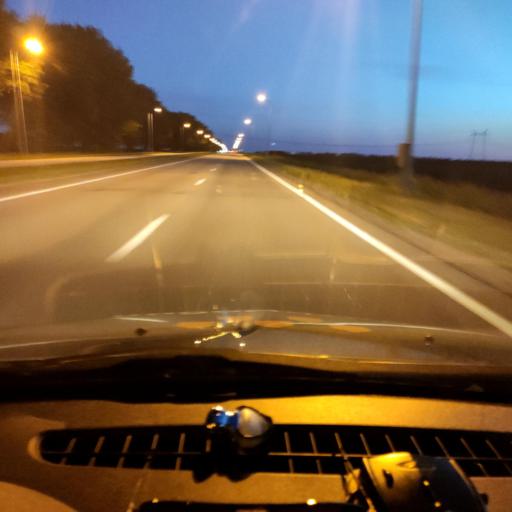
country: RU
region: Belgorod
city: Skorodnoye
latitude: 51.1787
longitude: 37.3414
